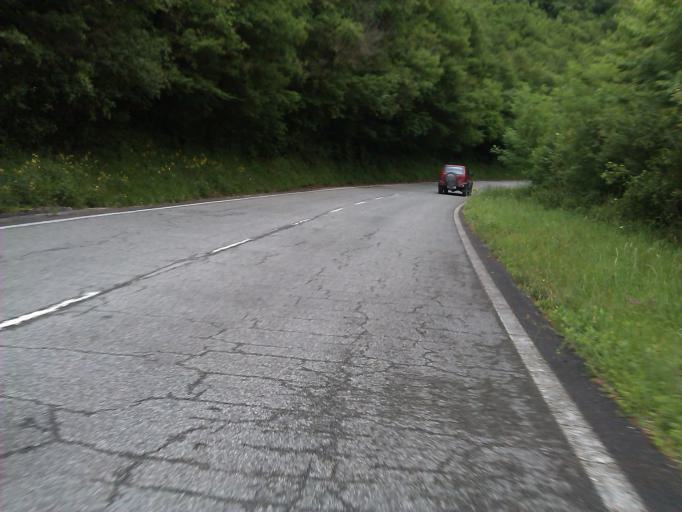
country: ES
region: Navarre
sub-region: Provincia de Navarra
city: Irurtzun
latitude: 42.9428
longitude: -1.8240
